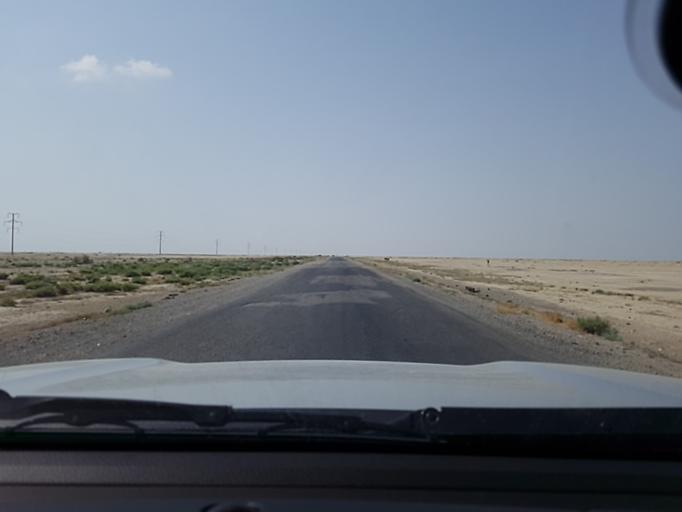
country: TM
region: Balkan
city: Gumdag
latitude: 38.8958
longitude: 54.5926
